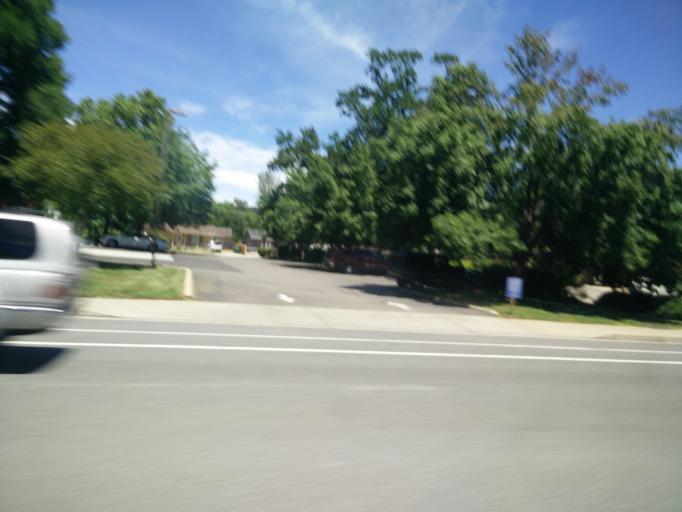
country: US
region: California
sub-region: Shasta County
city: Shasta Lake
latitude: 40.6804
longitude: -122.3614
